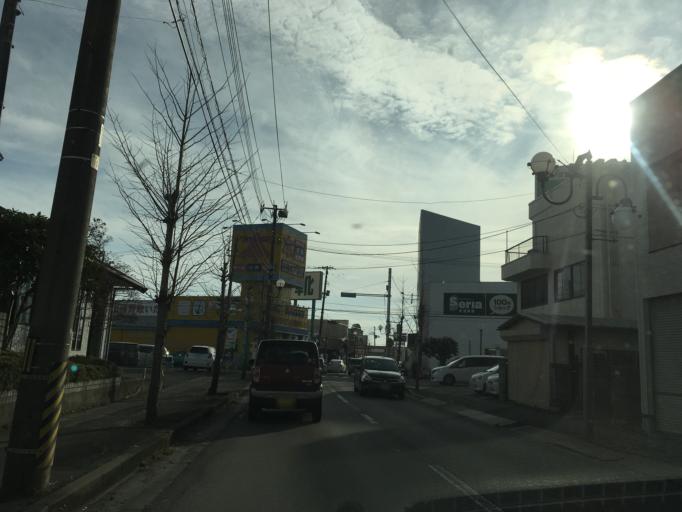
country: JP
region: Miyagi
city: Wakuya
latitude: 38.6921
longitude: 141.1910
